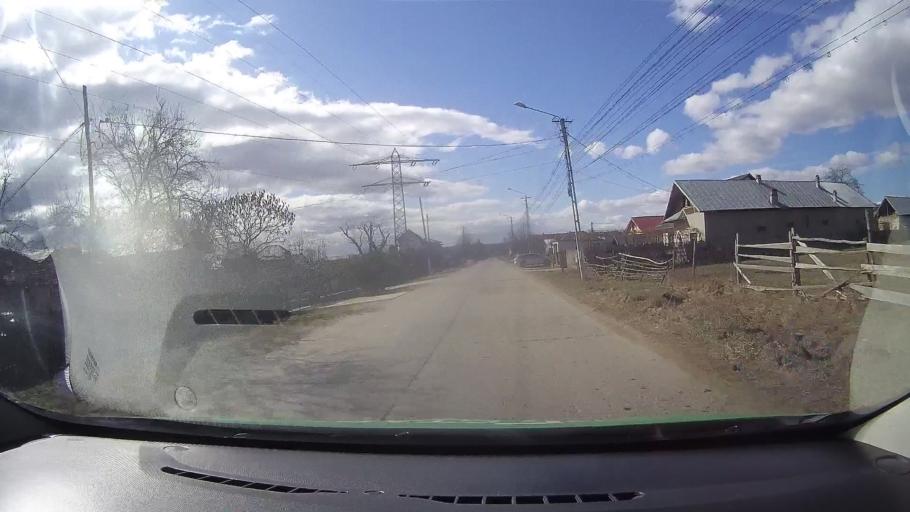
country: RO
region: Dambovita
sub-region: Comuna Vulcana-Pandele
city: Gura Vulcanei
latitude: 45.0252
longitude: 25.4043
